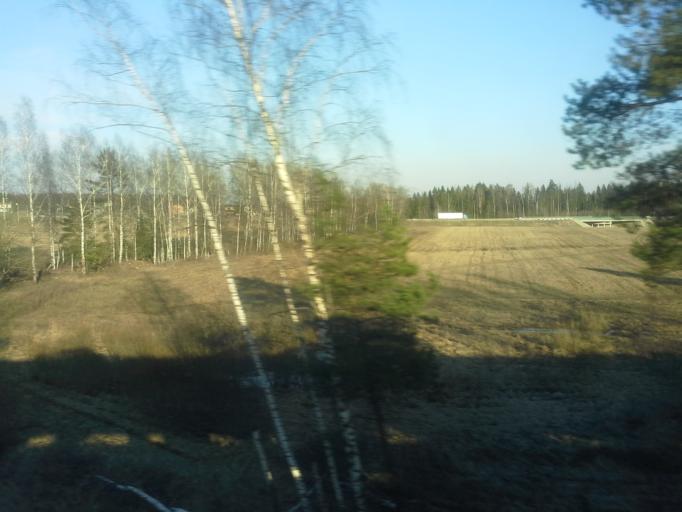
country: RU
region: Moskovskaya
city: Nekrasovskiy
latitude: 56.1055
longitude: 37.5138
